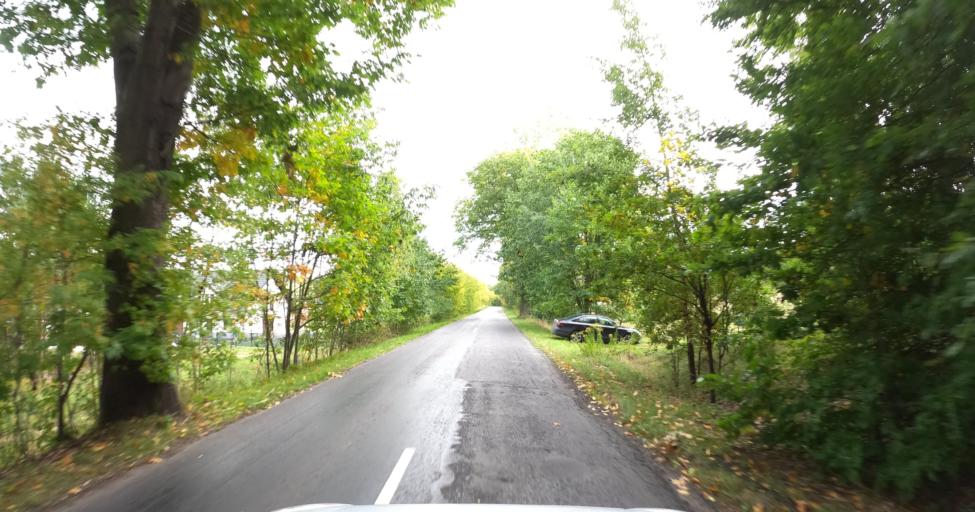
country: PL
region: Lubusz
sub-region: Powiat zielonogorski
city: Zabor
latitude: 51.9475
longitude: 15.6448
